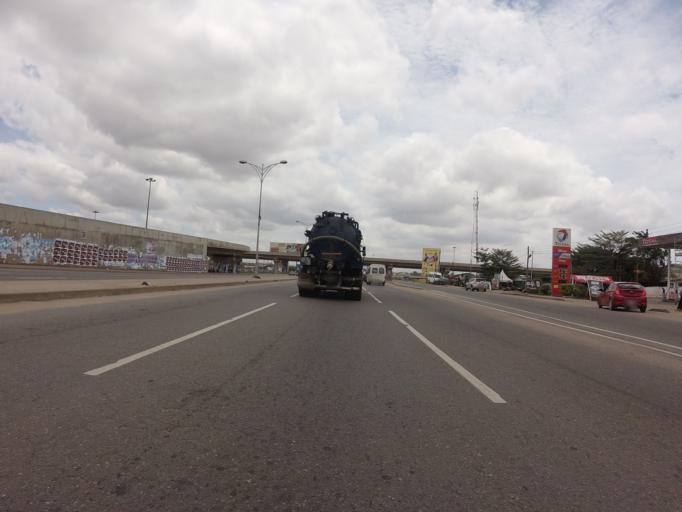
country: GH
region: Greater Accra
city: Gbawe
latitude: 5.5700
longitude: -0.2852
